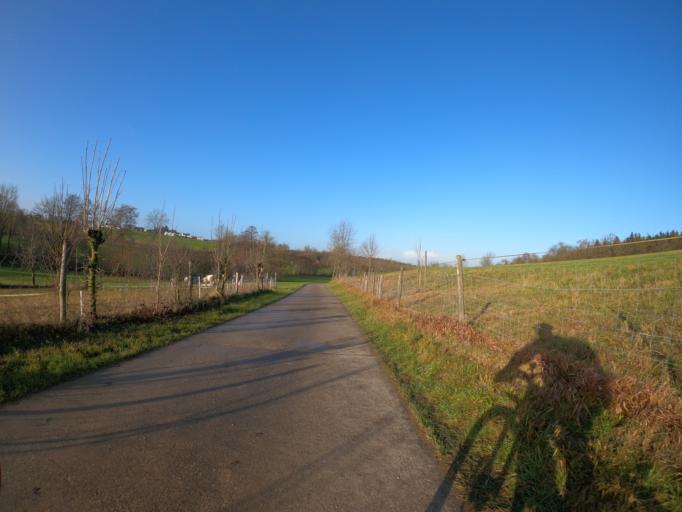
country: DE
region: Baden-Wuerttemberg
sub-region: Regierungsbezirk Stuttgart
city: Zell unter Aichelberg
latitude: 48.6554
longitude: 9.5840
